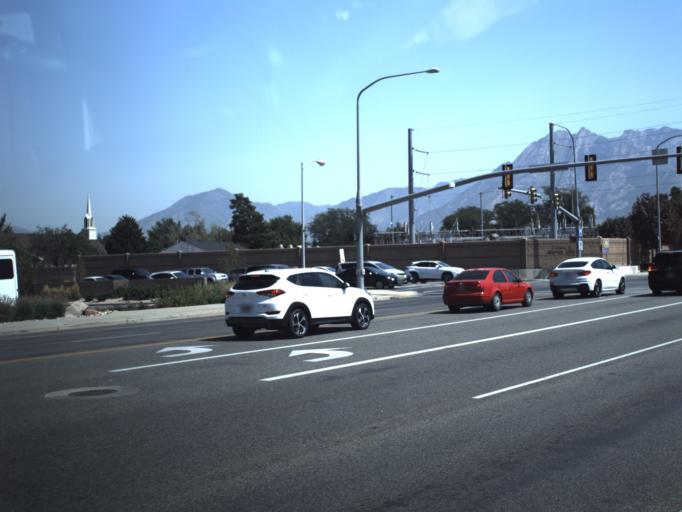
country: US
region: Utah
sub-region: Salt Lake County
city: Midvale
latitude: 40.6328
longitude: -111.8841
